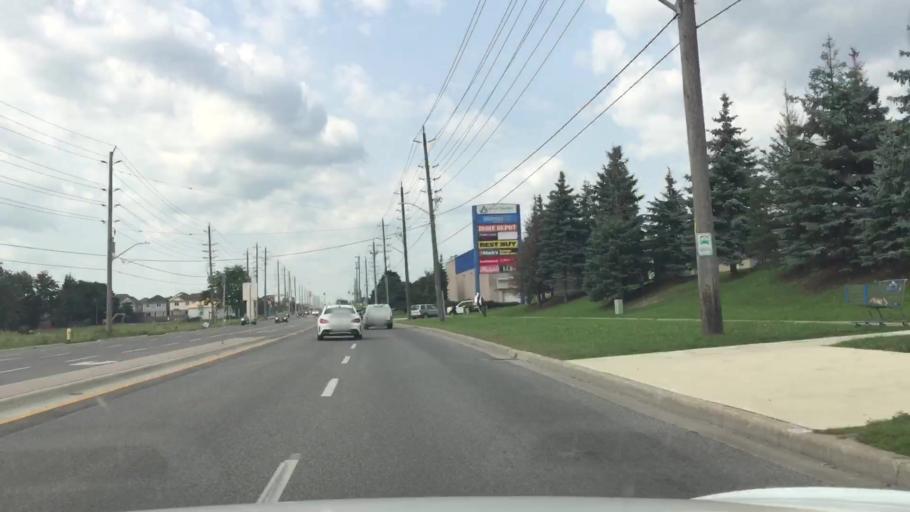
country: CA
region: Ontario
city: Oshawa
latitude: 43.9401
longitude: -78.8496
